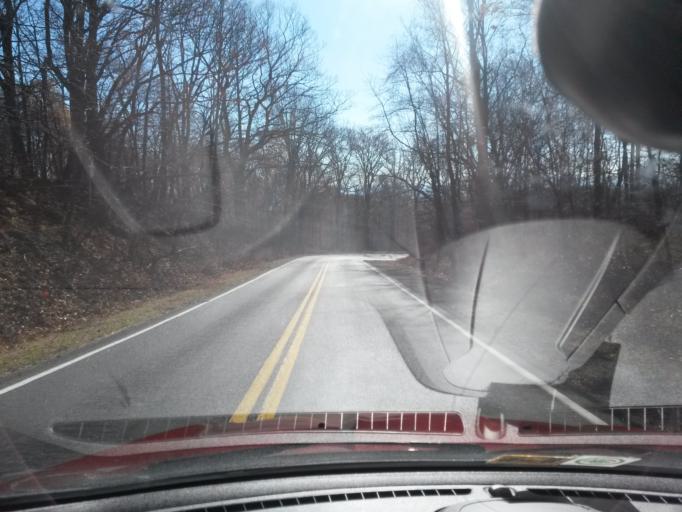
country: US
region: Virginia
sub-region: City of Bedford
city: Bedford
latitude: 37.4390
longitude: -79.5855
